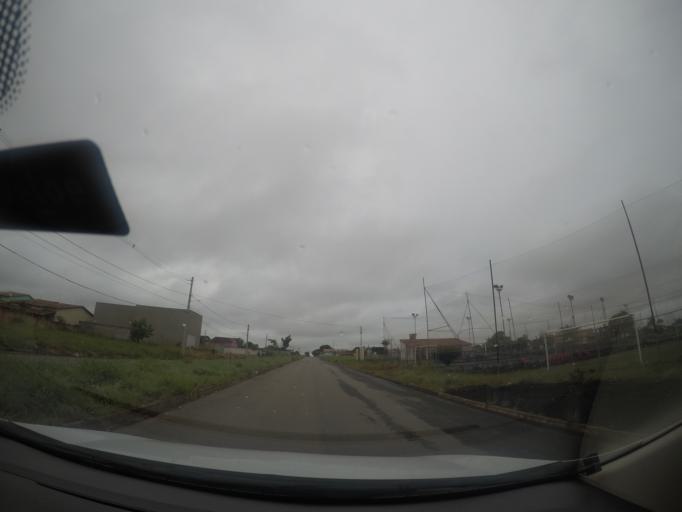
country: BR
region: Goias
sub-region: Goiania
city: Goiania
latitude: -16.7555
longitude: -49.3176
